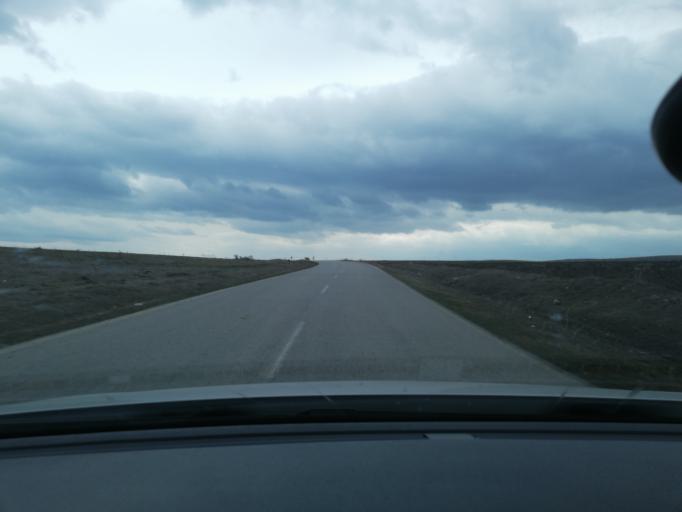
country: TR
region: Bolu
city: Gerede
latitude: 40.7262
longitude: 32.2220
